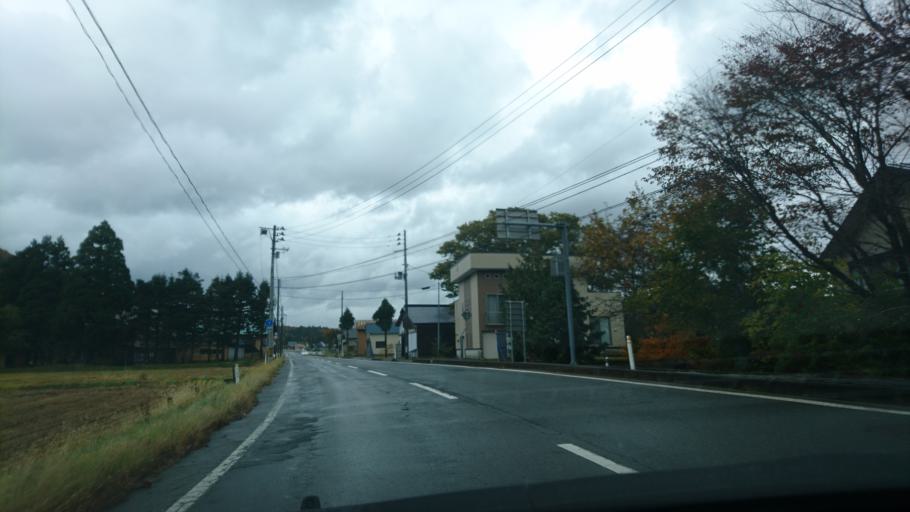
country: JP
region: Akita
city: Kakunodatemachi
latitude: 39.4821
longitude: 140.8034
